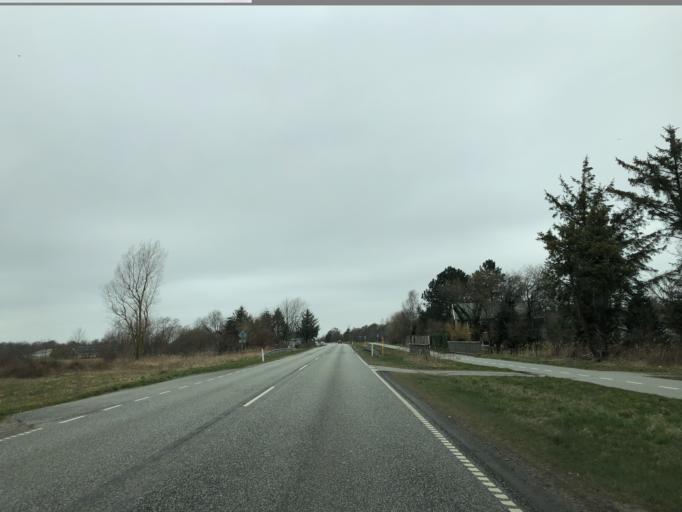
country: DK
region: North Denmark
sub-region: Frederikshavn Kommune
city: Strandby
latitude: 57.4649
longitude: 10.5138
